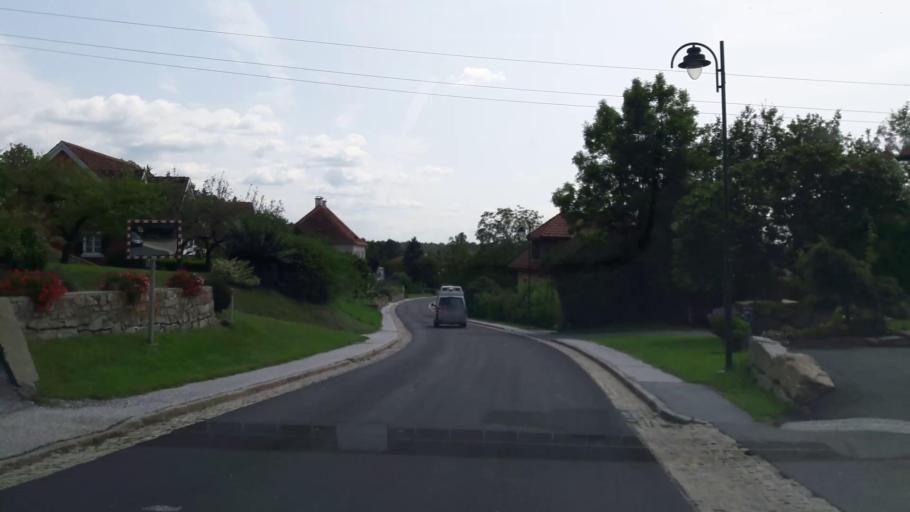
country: AT
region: Styria
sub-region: Politischer Bezirk Hartberg-Fuerstenfeld
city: Stubenberg
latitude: 47.2424
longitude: 15.8027
